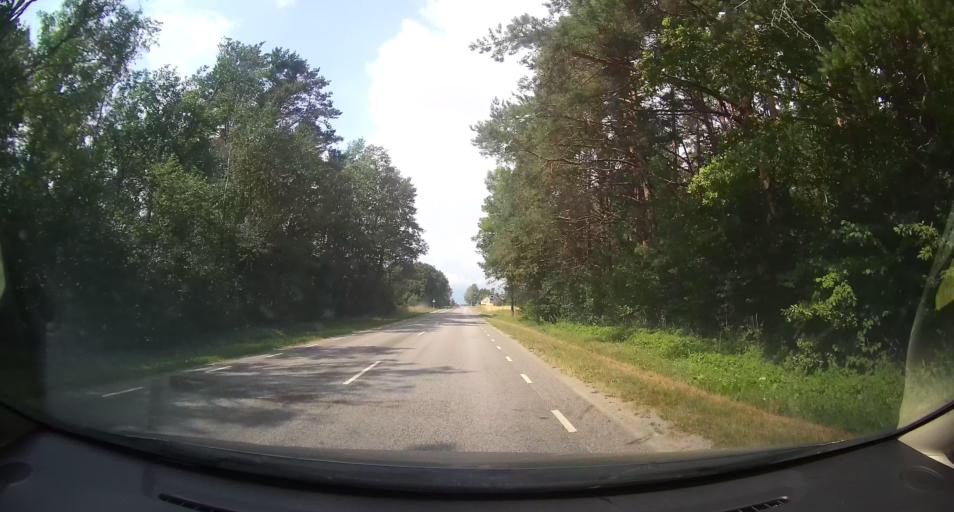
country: EE
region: Laeaene
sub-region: Lihula vald
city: Lihula
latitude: 58.5702
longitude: 23.7505
